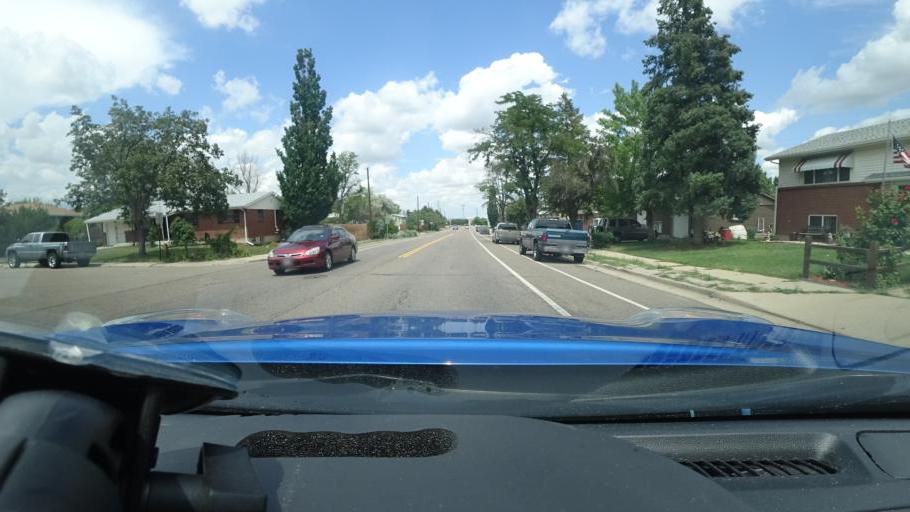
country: US
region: Colorado
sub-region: Adams County
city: Aurora
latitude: 39.7060
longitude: -104.8294
